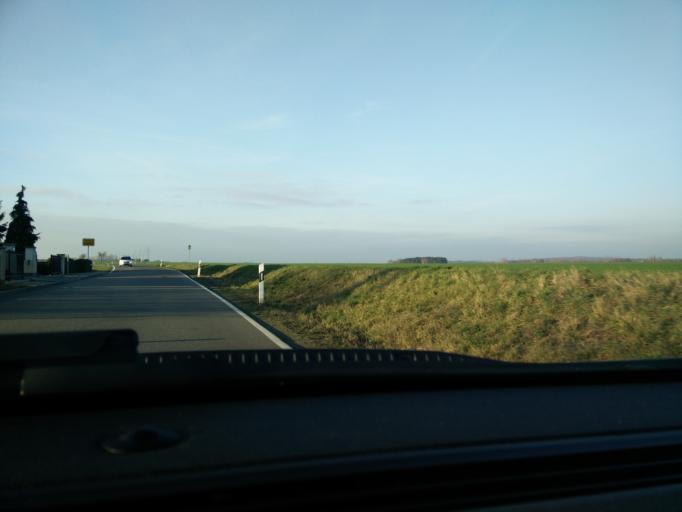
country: DE
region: Saxony
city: Grossbardau
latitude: 51.2063
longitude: 12.6925
